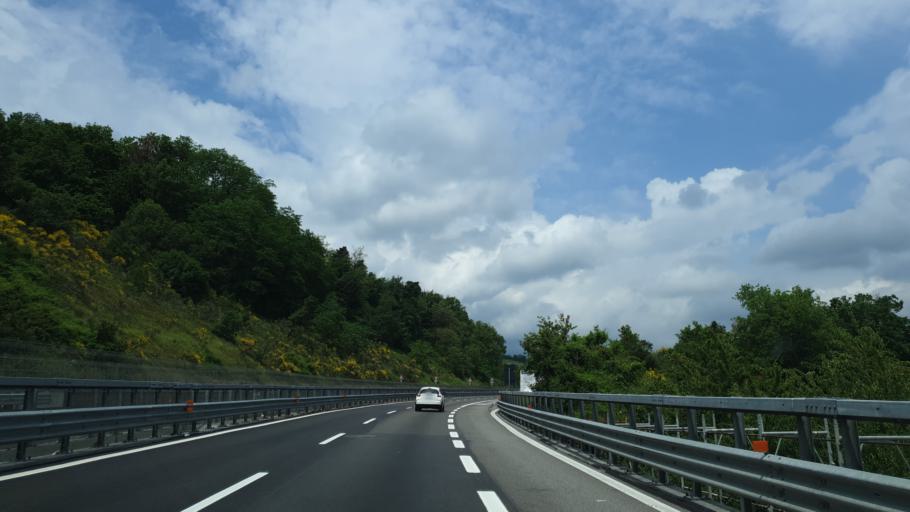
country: IT
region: Tuscany
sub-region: Province of Florence
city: Barberino di Mugello
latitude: 44.0000
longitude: 11.2188
